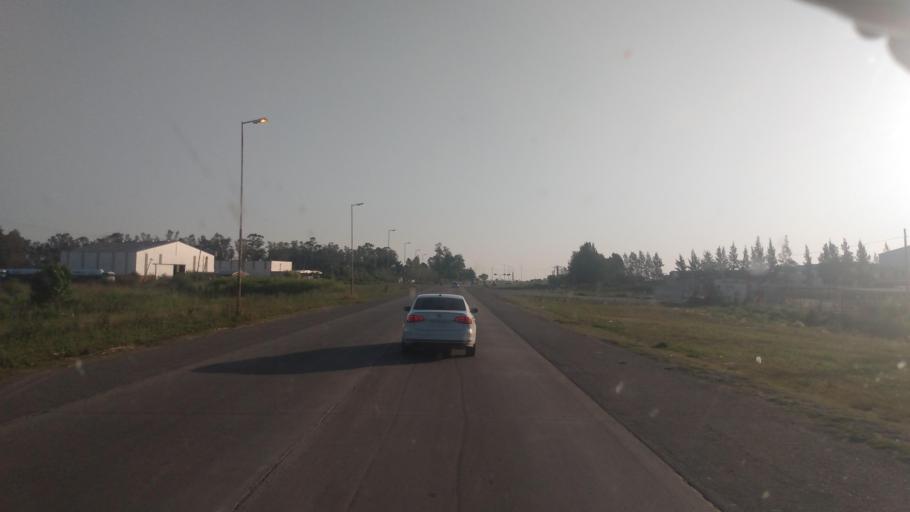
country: AR
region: Buenos Aires
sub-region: Partido de Campana
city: Campana
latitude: -34.1985
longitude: -58.9549
